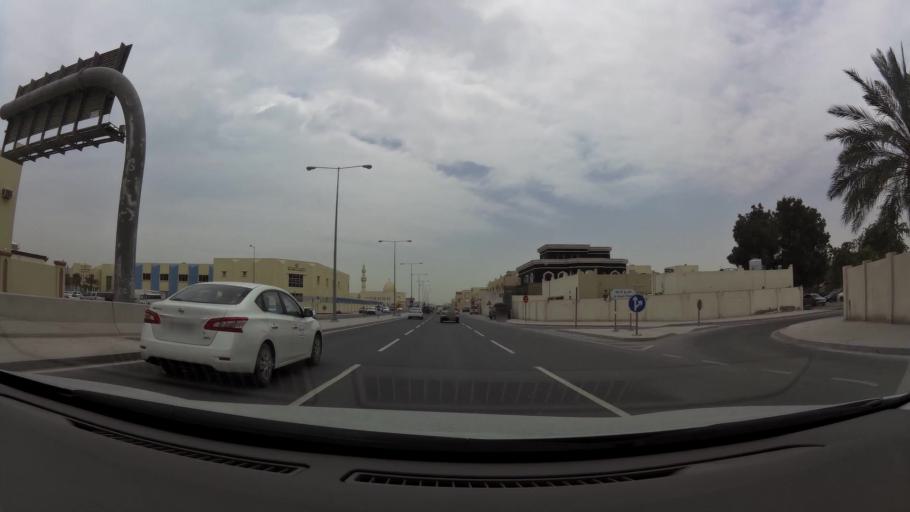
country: QA
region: Baladiyat ar Rayyan
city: Ar Rayyan
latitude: 25.2422
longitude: 51.4648
